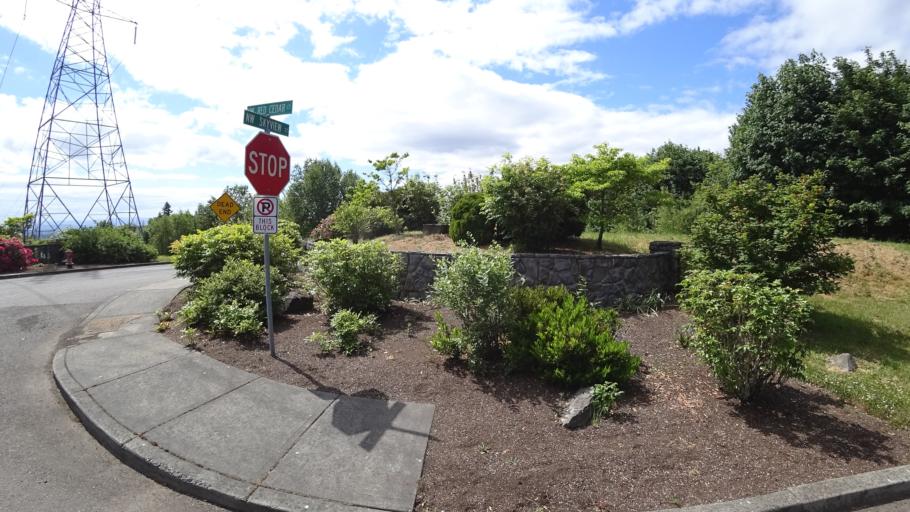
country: US
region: Oregon
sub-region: Washington County
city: Bethany
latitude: 45.5925
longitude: -122.8299
